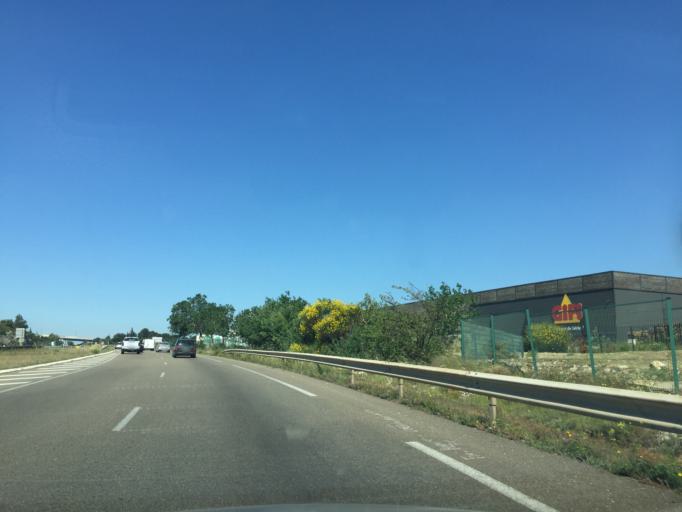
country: FR
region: Languedoc-Roussillon
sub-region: Departement du Gard
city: Les Angles
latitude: 43.9578
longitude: 4.7521
